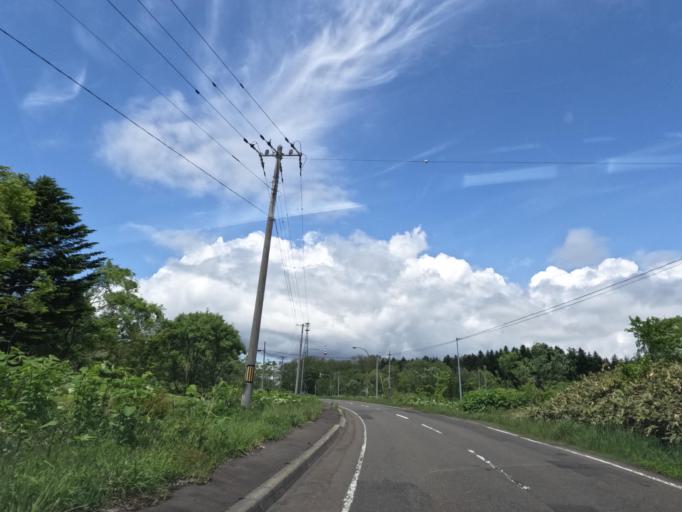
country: JP
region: Hokkaido
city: Tobetsu
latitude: 43.3996
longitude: 141.5816
